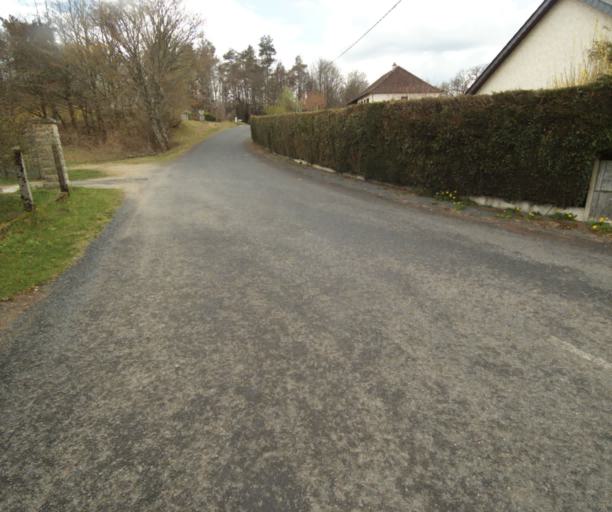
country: FR
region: Limousin
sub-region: Departement de la Correze
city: Correze
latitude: 45.3354
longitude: 1.9395
